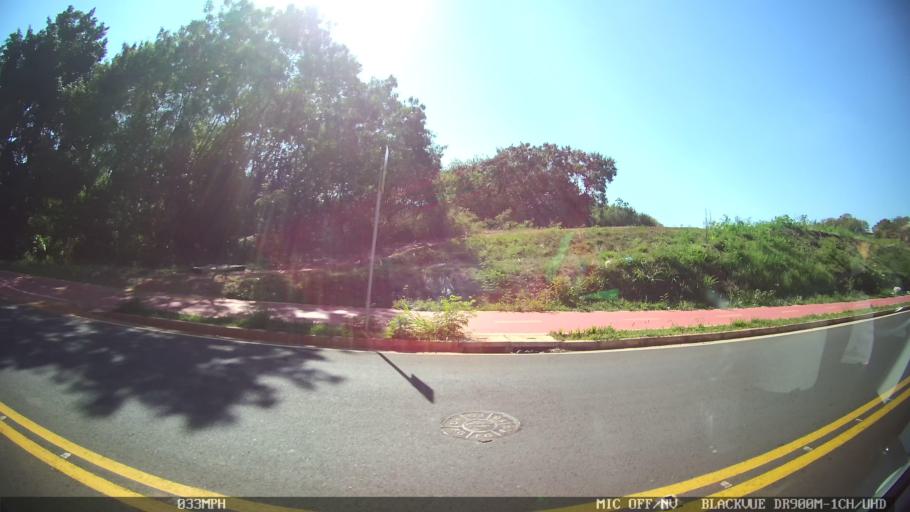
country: BR
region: Sao Paulo
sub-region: Sao Jose Do Rio Preto
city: Sao Jose do Rio Preto
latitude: -20.8072
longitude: -49.4232
